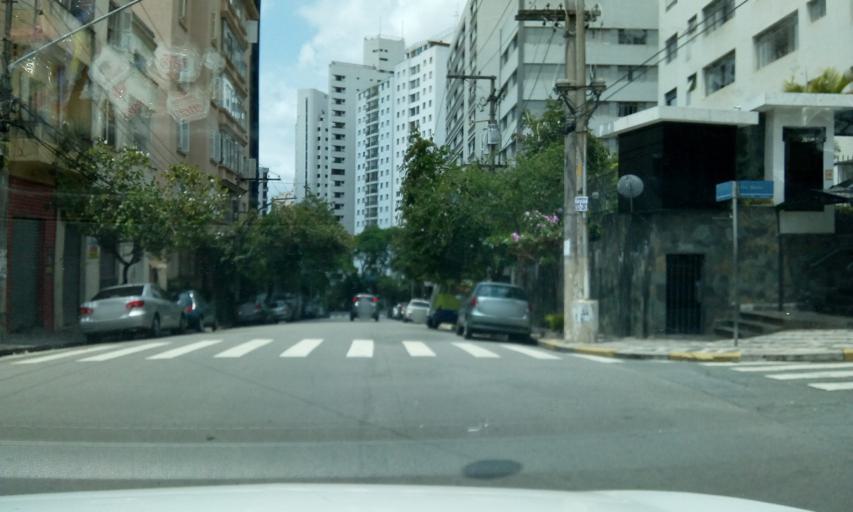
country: BR
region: Sao Paulo
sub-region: Sao Paulo
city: Sao Paulo
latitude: -23.5695
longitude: -46.6338
